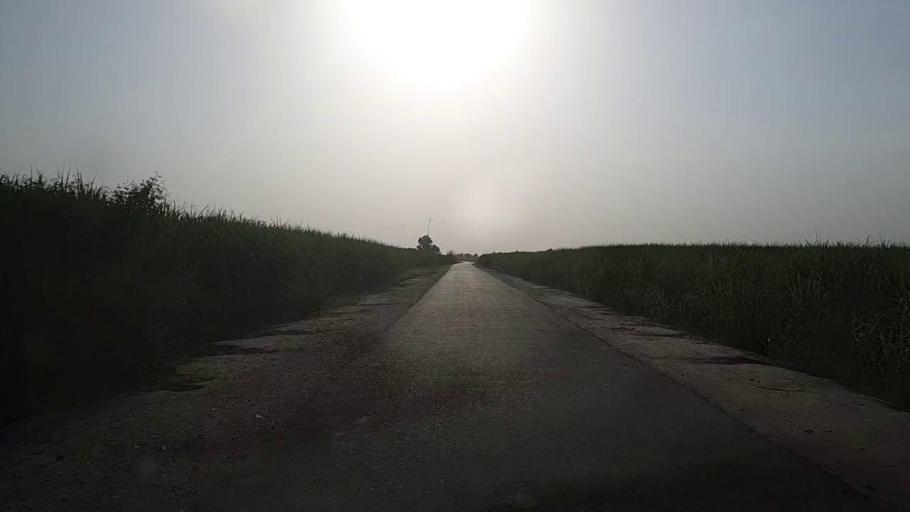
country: PK
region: Sindh
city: Ubauro
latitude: 28.0999
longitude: 69.8228
